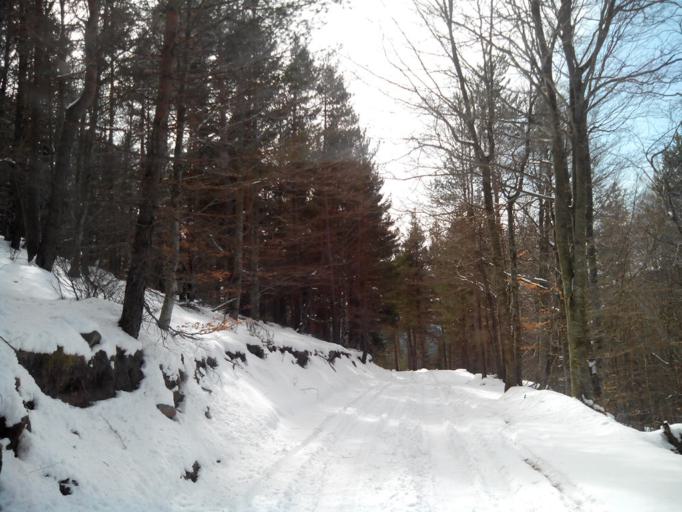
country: ES
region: Catalonia
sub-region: Provincia de Barcelona
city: Sant Julia de Cerdanyola
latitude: 42.1962
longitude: 1.9281
